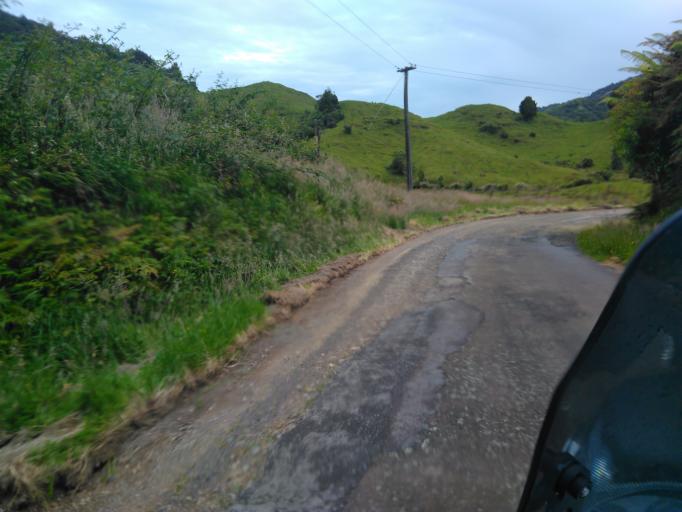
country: NZ
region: Bay of Plenty
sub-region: Opotiki District
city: Opotiki
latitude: -38.1144
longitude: 177.5055
